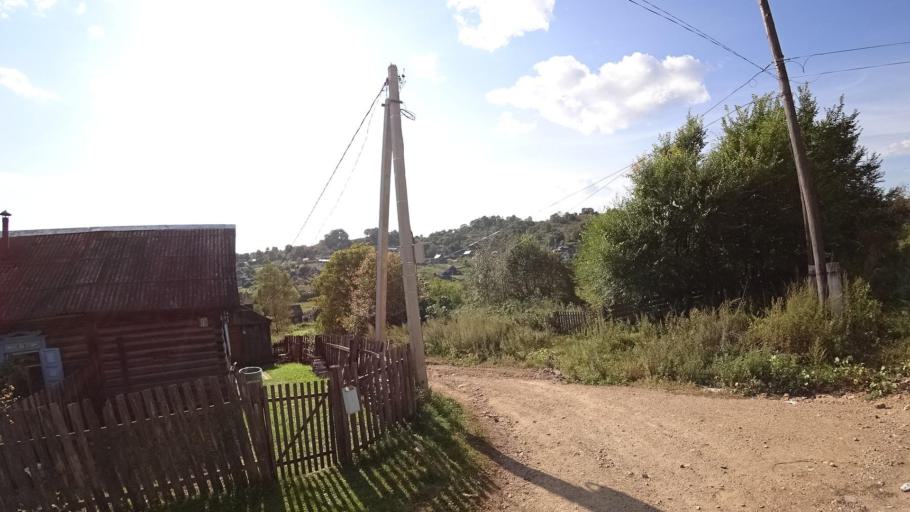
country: RU
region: Jewish Autonomous Oblast
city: Birakan
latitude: 48.9973
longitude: 131.7226
